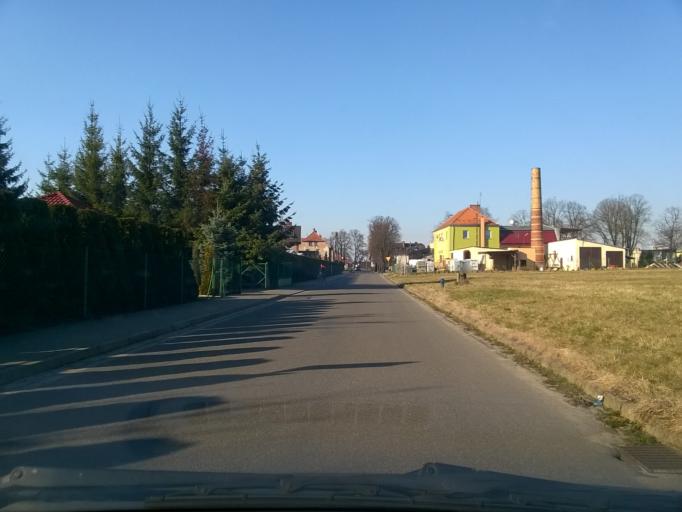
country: PL
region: Greater Poland Voivodeship
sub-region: Powiat wagrowiecki
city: Golancz
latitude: 52.9449
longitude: 17.3062
